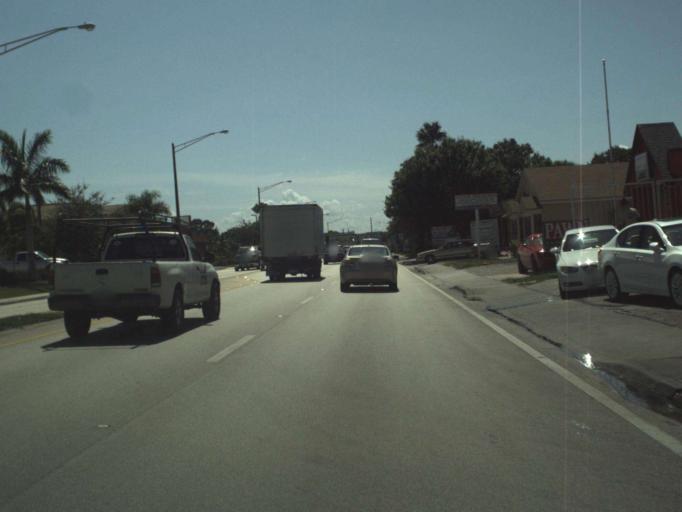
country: US
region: Florida
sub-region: Indian River County
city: Vero Beach
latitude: 27.6398
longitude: -80.3902
